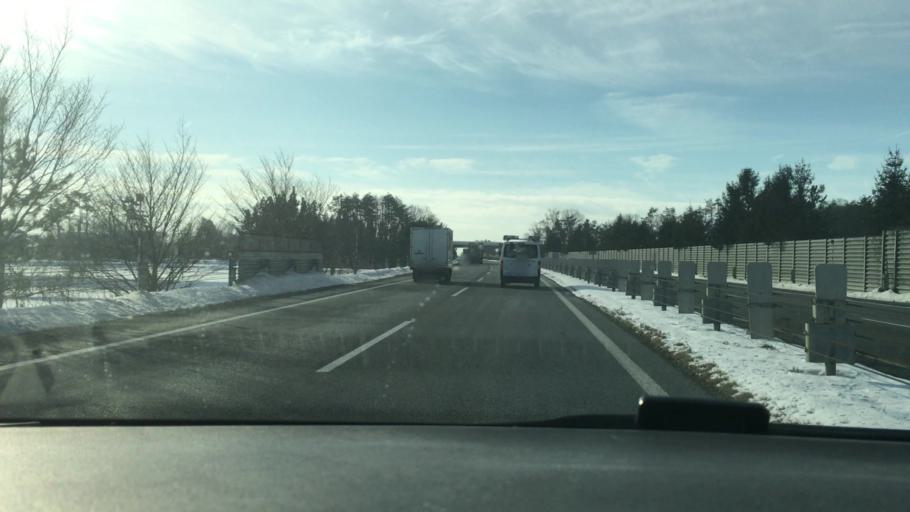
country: JP
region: Iwate
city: Hanamaki
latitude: 39.4048
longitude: 141.0925
